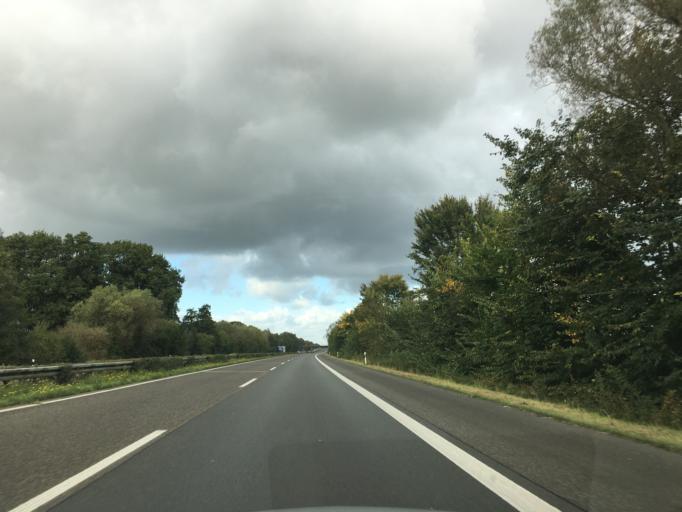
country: DE
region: North Rhine-Westphalia
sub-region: Regierungsbezirk Dusseldorf
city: Sonsbeck
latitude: 51.5934
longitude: 6.3695
